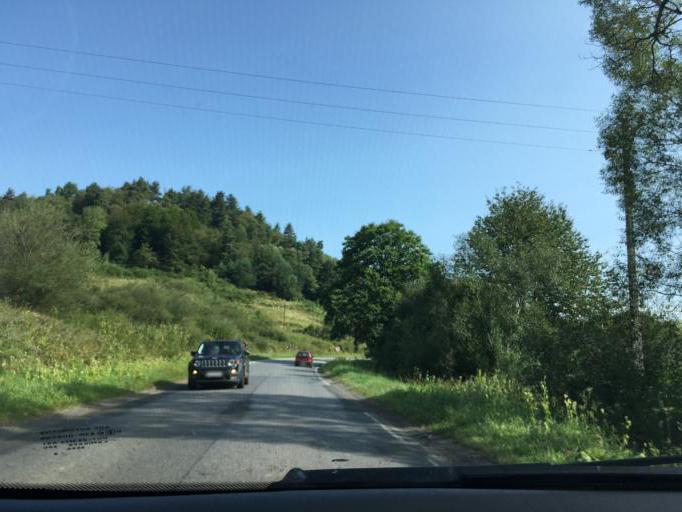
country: PL
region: Subcarpathian Voivodeship
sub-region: Powiat bieszczadzki
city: Ustrzyki Dolne
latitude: 49.3870
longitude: 22.6357
